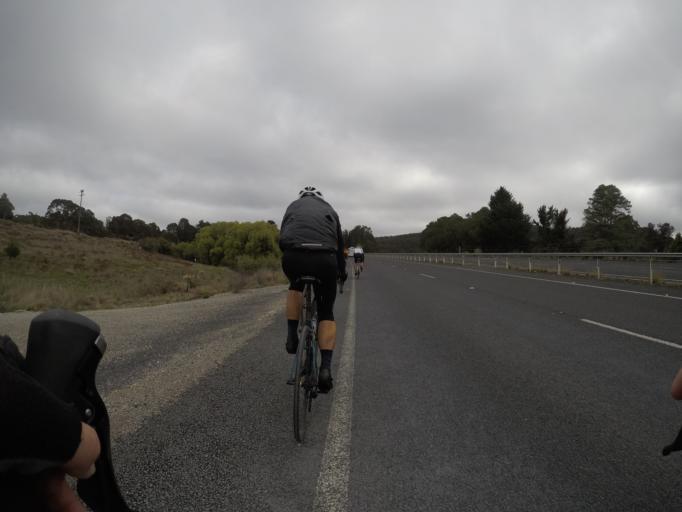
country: AU
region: New South Wales
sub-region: Lithgow
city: Lithgow
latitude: -33.4344
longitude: 150.1124
